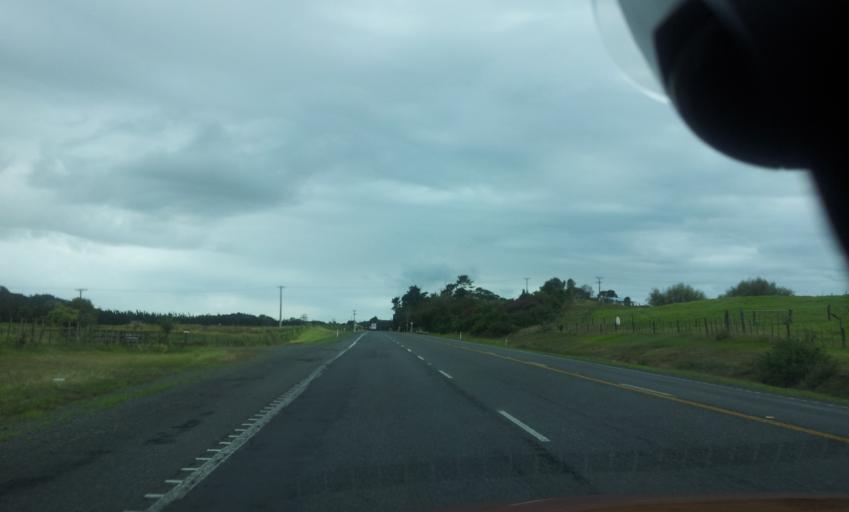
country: NZ
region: Northland
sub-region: Whangarei
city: Ruakaka
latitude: -35.9529
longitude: 174.4527
